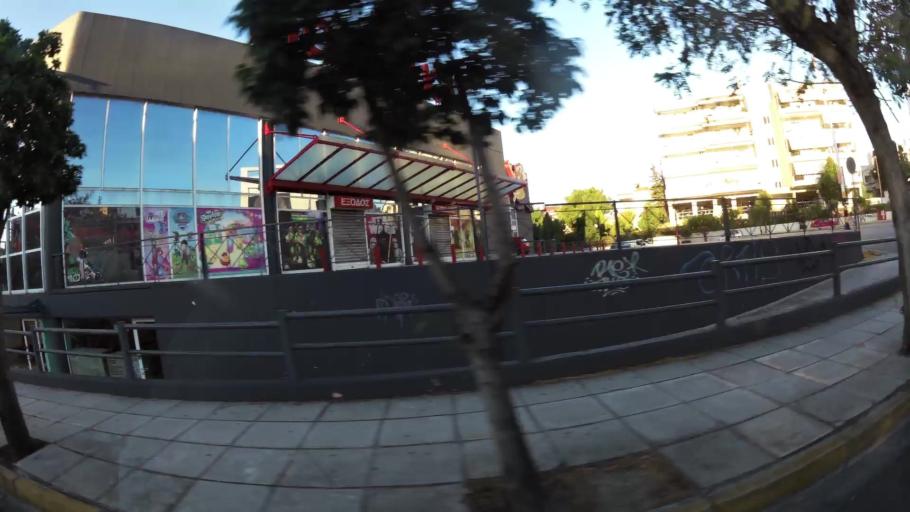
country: GR
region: Attica
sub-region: Nomarchia Athinas
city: Melissia
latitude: 38.0496
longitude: 23.8396
